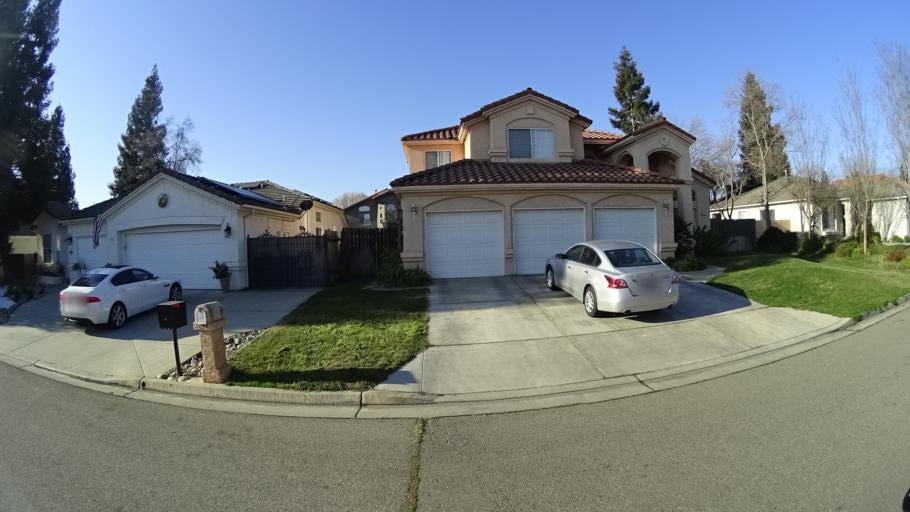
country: US
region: California
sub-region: Fresno County
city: Clovis
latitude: 36.8750
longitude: -119.7433
